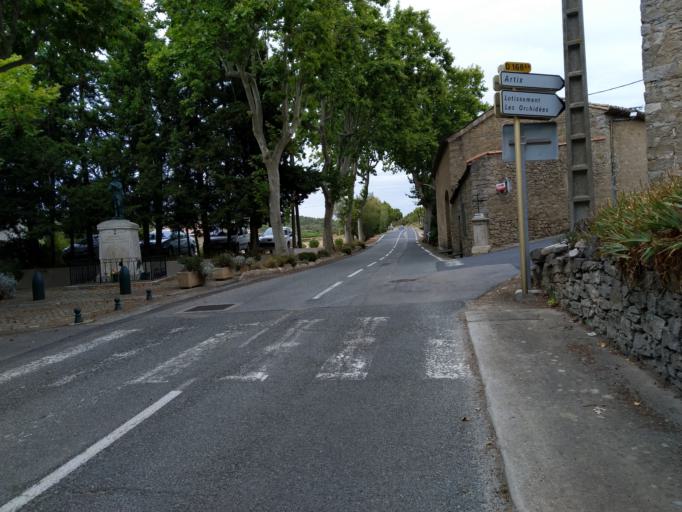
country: FR
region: Languedoc-Roussillon
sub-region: Departement de l'Herault
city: Olonzac
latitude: 43.2994
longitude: 2.7595
